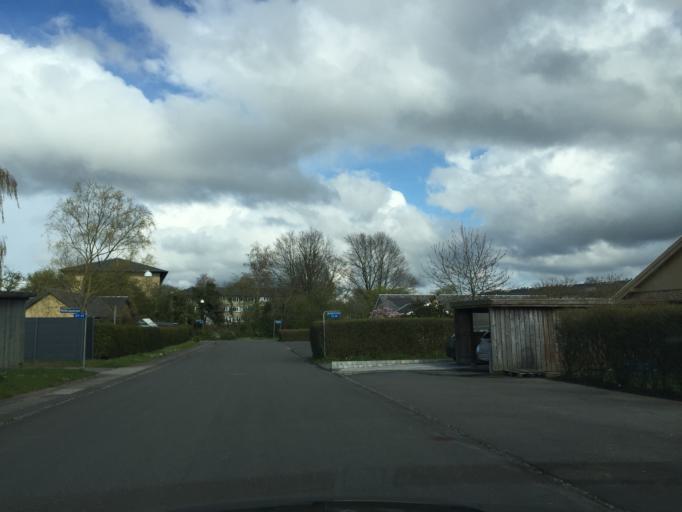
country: DK
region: South Denmark
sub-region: Odense Kommune
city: Neder Holluf
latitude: 55.3765
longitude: 10.4196
